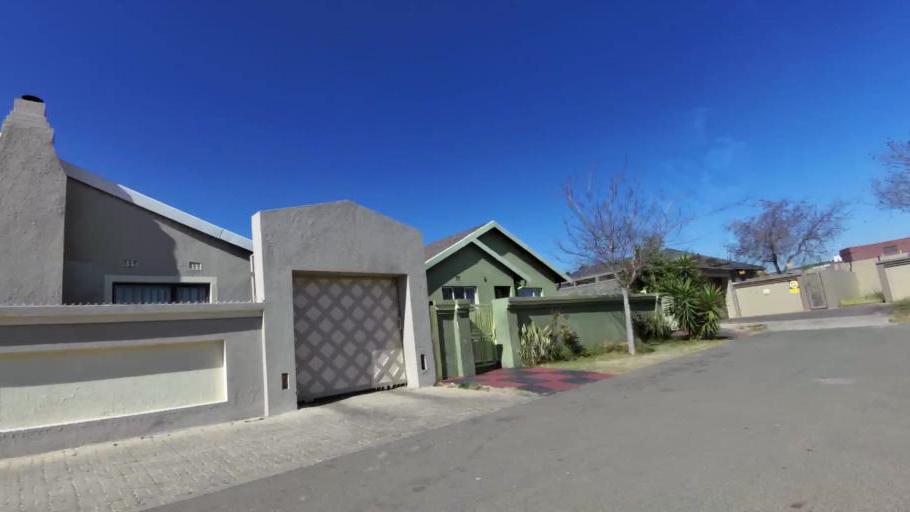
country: ZA
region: Gauteng
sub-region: City of Johannesburg Metropolitan Municipality
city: Johannesburg
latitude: -26.2505
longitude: 27.9789
